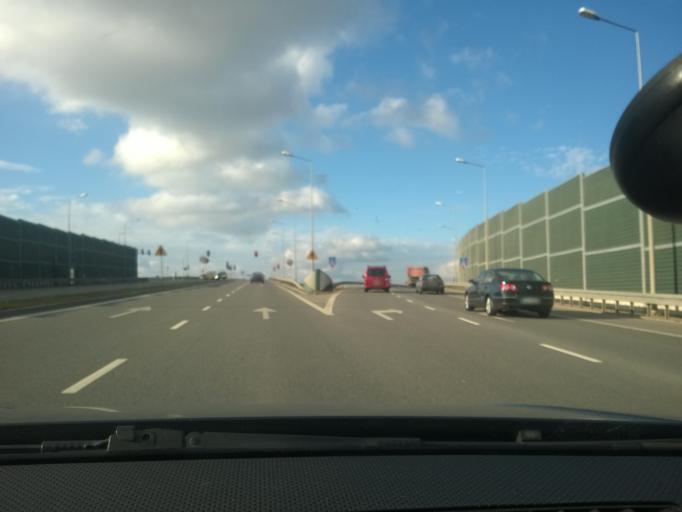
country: PL
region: Masovian Voivodeship
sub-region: Powiat warszawski zachodni
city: Ozarow Mazowiecki
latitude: 52.1857
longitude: 20.7799
